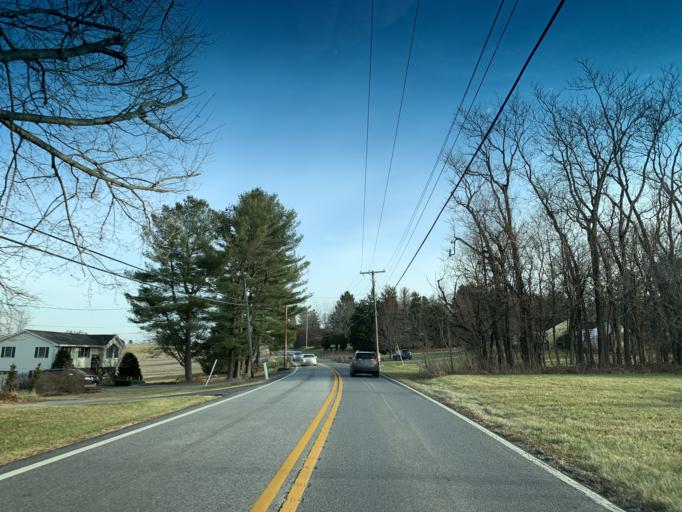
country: US
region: Maryland
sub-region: Baltimore County
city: Hunt Valley
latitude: 39.5855
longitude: -76.7240
